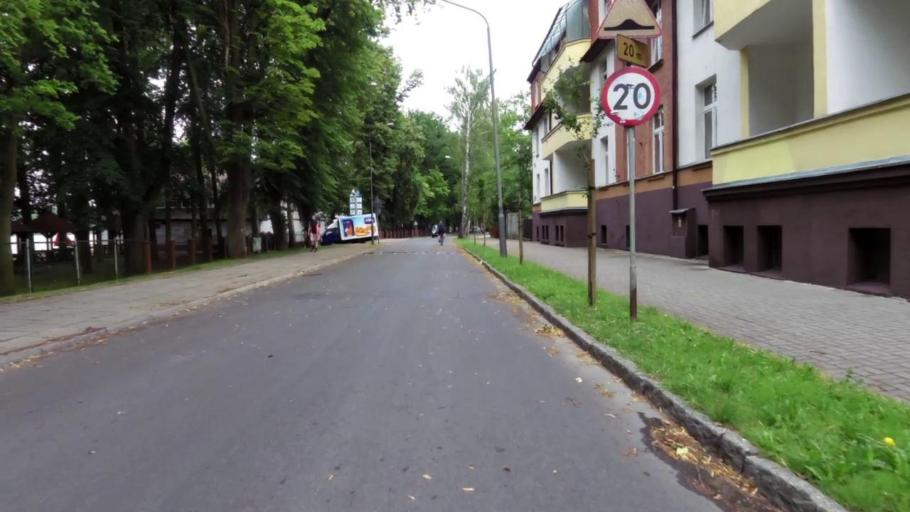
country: PL
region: West Pomeranian Voivodeship
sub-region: Powiat mysliborski
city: Mysliborz
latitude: 52.9238
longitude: 14.8596
